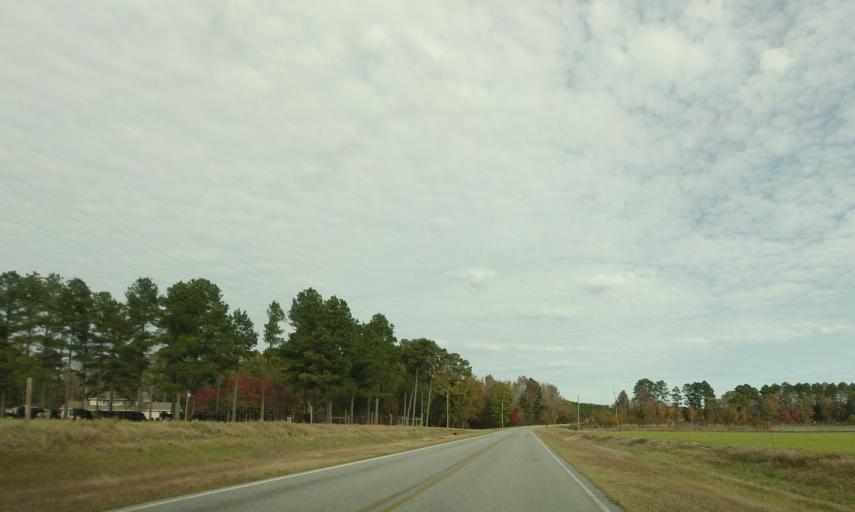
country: US
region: Georgia
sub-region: Dodge County
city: Chester
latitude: 32.4739
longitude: -83.1061
